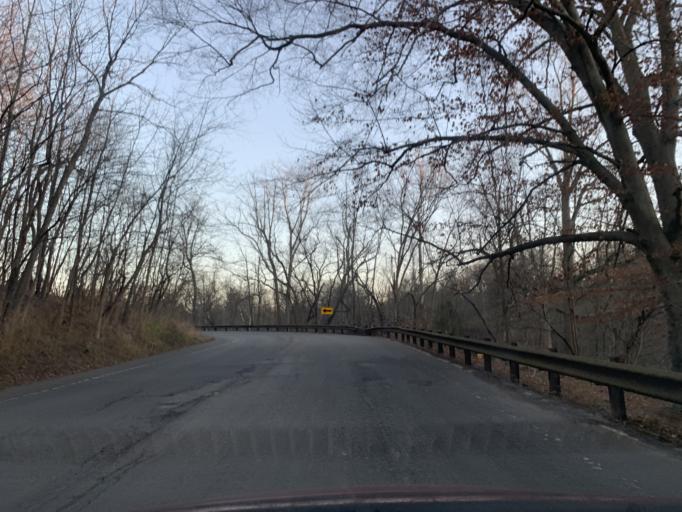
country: US
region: Kentucky
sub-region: Jefferson County
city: Saint Matthews
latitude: 38.2338
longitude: -85.6840
